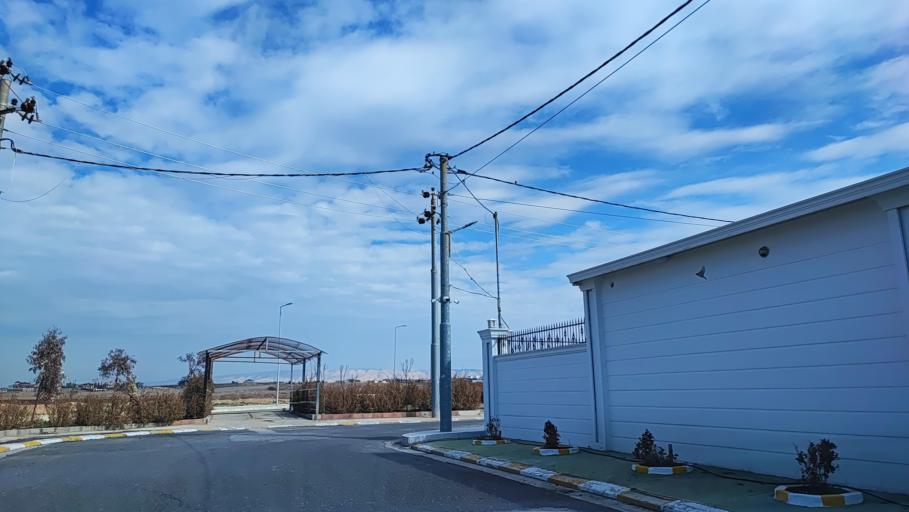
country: IQ
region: Arbil
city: Erbil
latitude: 36.2871
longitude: 44.0743
